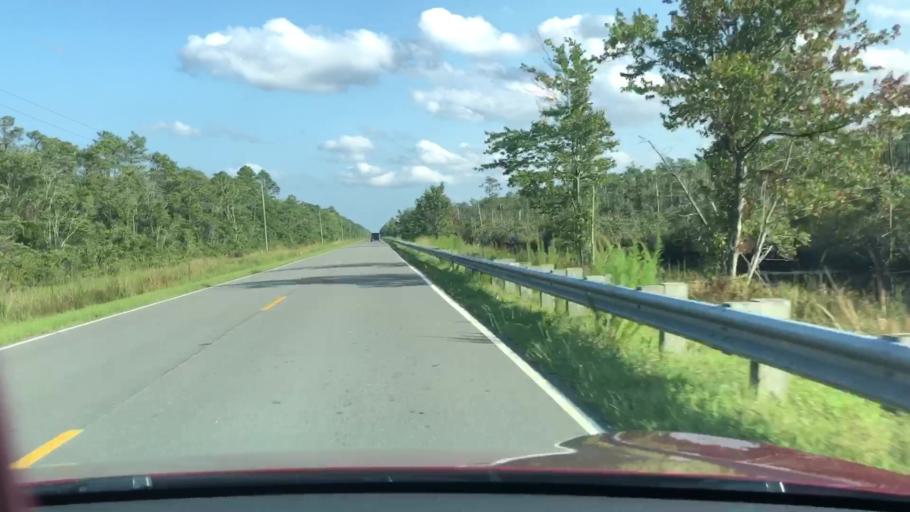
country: US
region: North Carolina
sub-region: Dare County
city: Manteo
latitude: 35.8100
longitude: -75.7904
